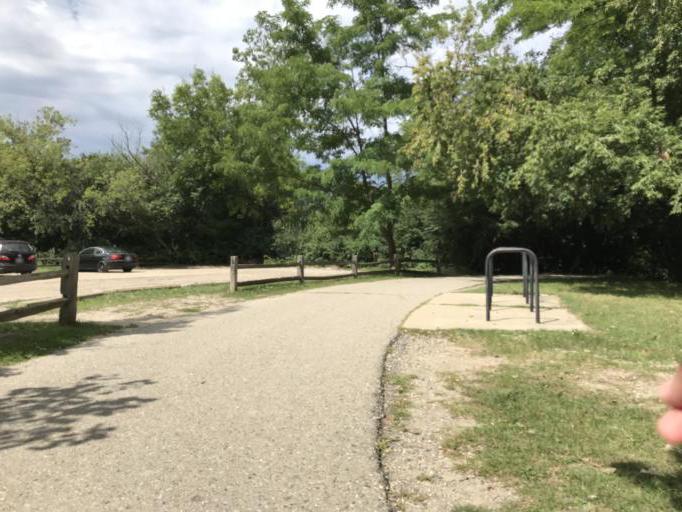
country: US
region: Michigan
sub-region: Washtenaw County
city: Ann Arbor
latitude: 42.2973
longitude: -83.7443
